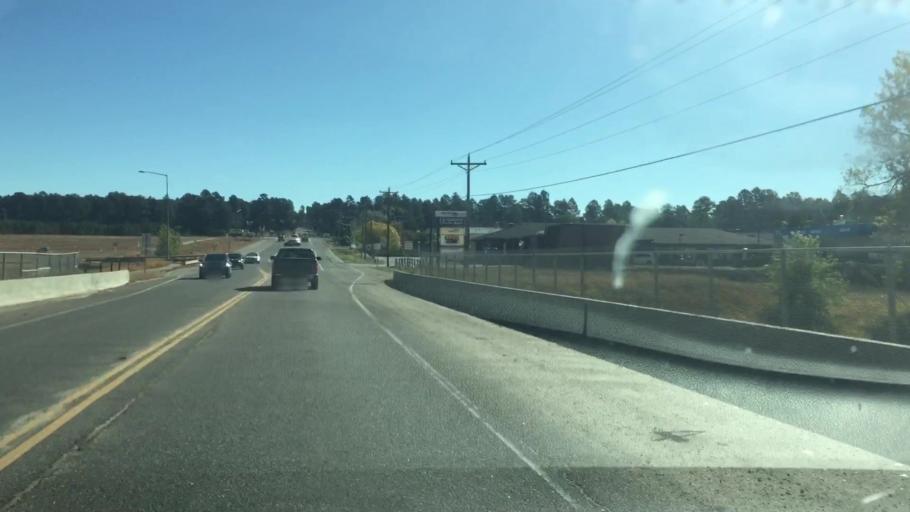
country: US
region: Colorado
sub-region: Elbert County
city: Elizabeth
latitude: 39.3615
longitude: -104.5936
